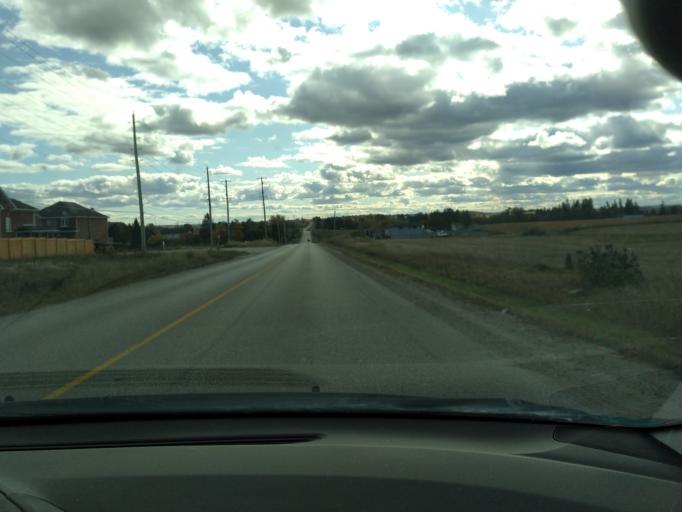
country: CA
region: Ontario
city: Bradford West Gwillimbury
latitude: 44.0995
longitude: -79.6001
